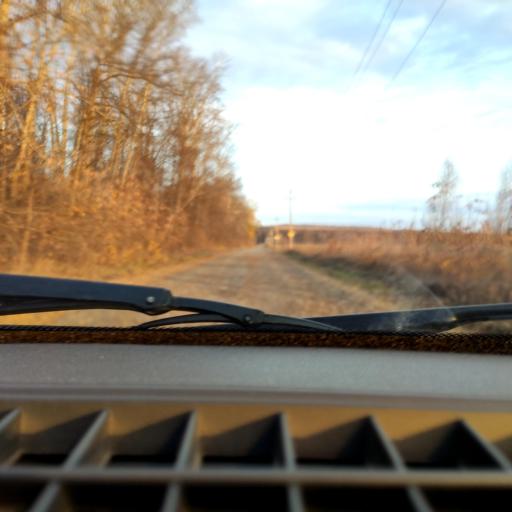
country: RU
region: Bashkortostan
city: Avdon
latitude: 54.6286
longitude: 55.7357
